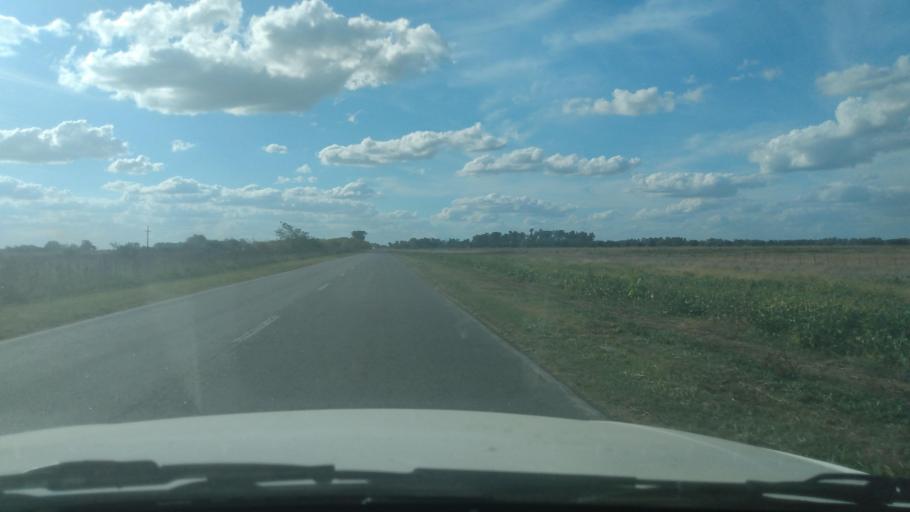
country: AR
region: Buenos Aires
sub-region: Partido de Navarro
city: Navarro
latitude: -34.9689
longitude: -59.3175
